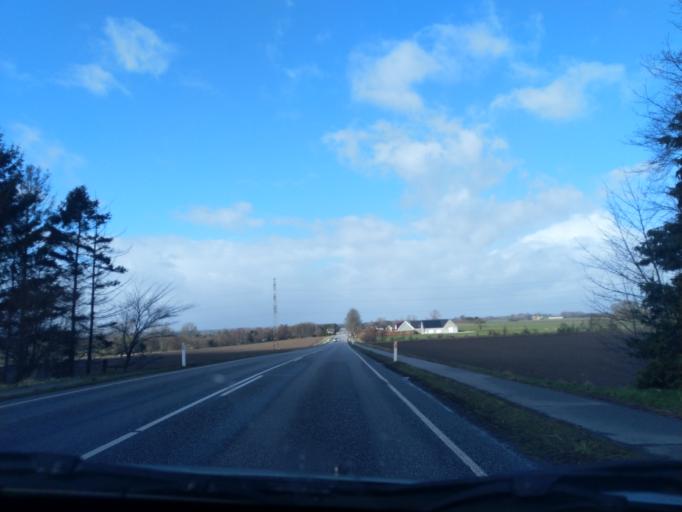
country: DK
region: Zealand
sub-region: Naestved Kommune
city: Naestved
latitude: 55.2777
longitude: 11.7233
